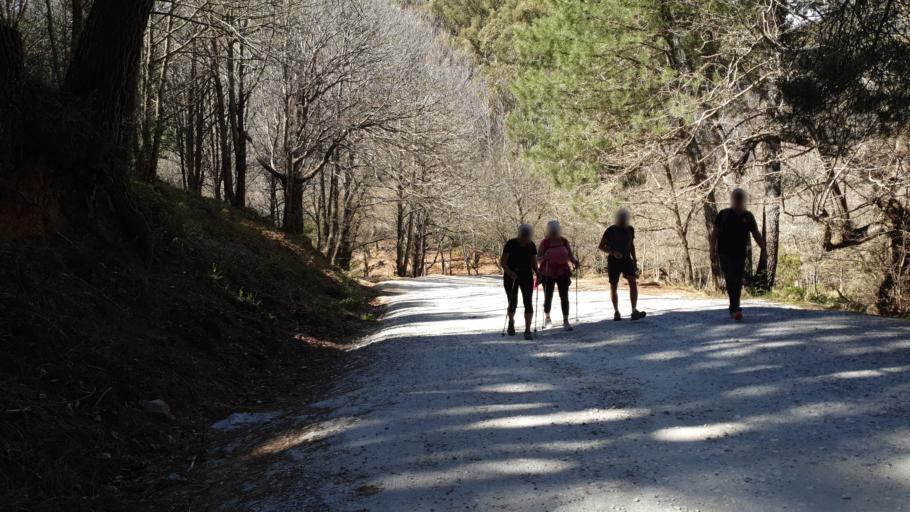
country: ES
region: Andalusia
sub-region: Provincia de Malaga
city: Ojen
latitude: 36.5778
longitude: -4.8836
